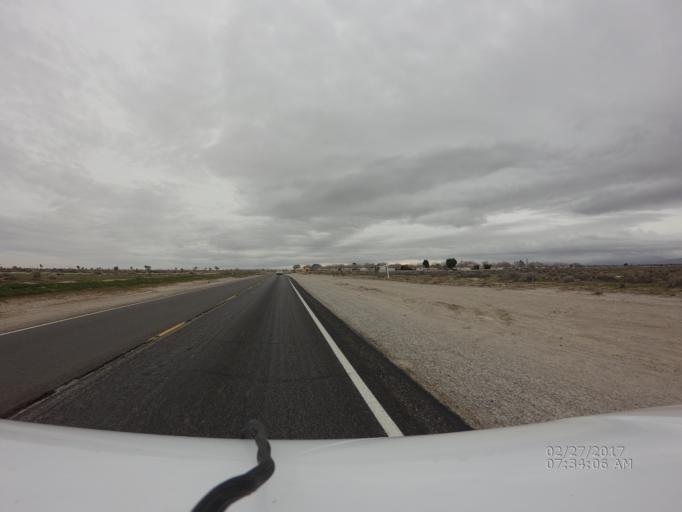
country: US
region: California
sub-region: Los Angeles County
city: Lancaster
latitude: 34.7188
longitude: -118.1152
